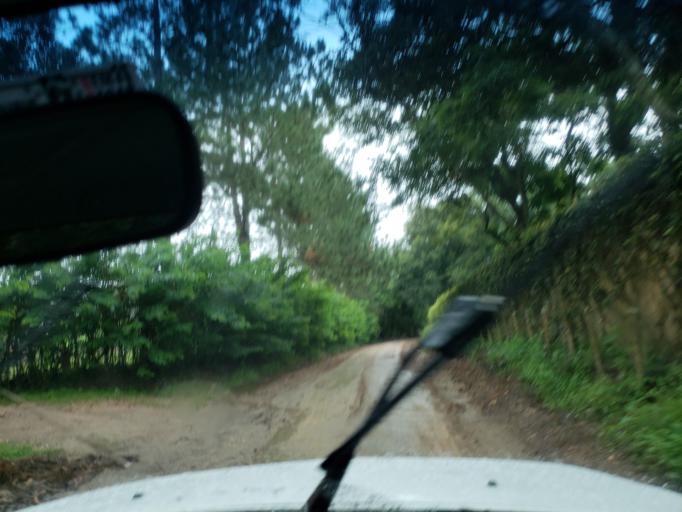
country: BR
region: Minas Gerais
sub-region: Monte Siao
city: Monte Siao
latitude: -22.3801
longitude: -46.5595
